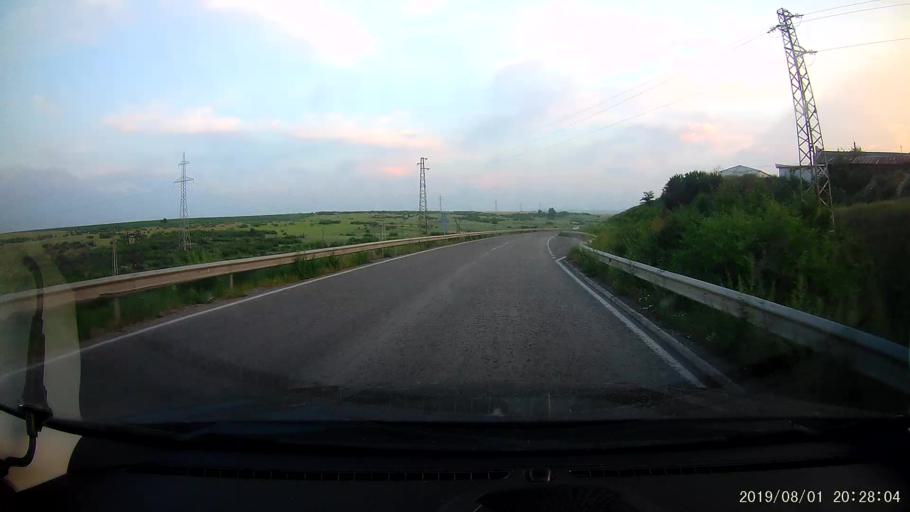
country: BG
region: Yambol
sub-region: Obshtina Elkhovo
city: Elkhovo
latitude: 42.1721
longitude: 26.5816
